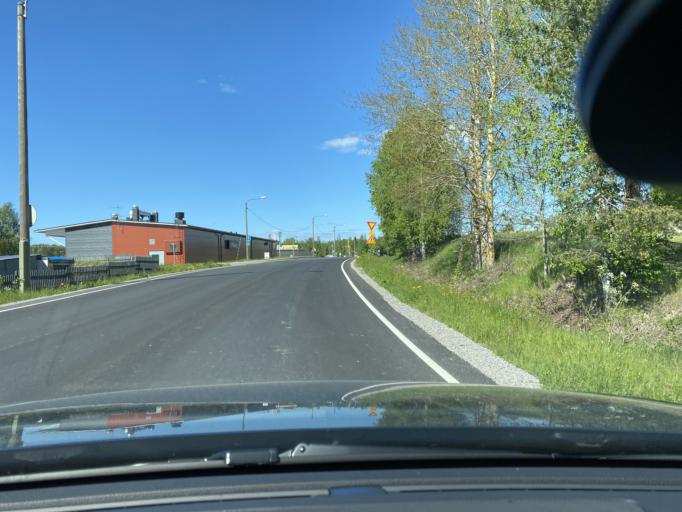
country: FI
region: Varsinais-Suomi
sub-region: Turku
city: Sauvo
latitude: 60.3406
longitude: 22.6866
